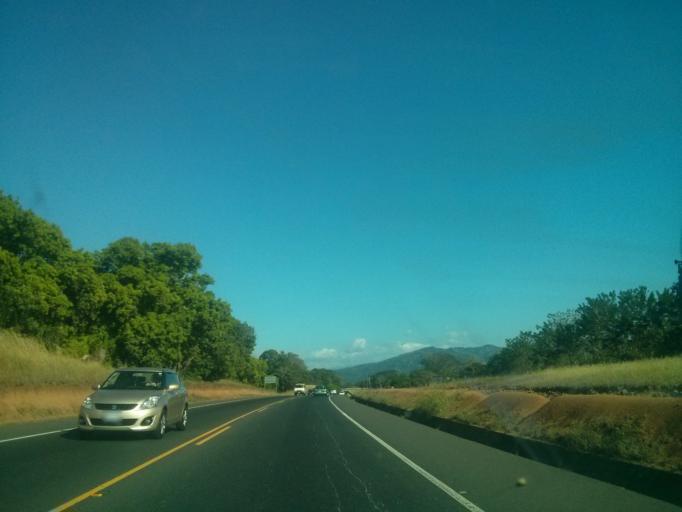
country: CR
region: Alajuela
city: Orotina
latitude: 9.9185
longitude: -84.4961
